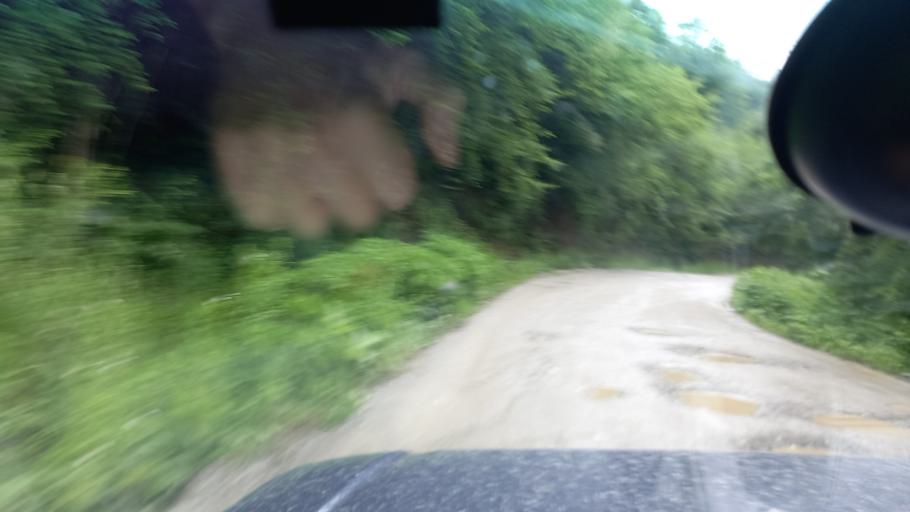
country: RU
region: Krasnodarskiy
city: Psebay
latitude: 44.0371
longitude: 40.7494
